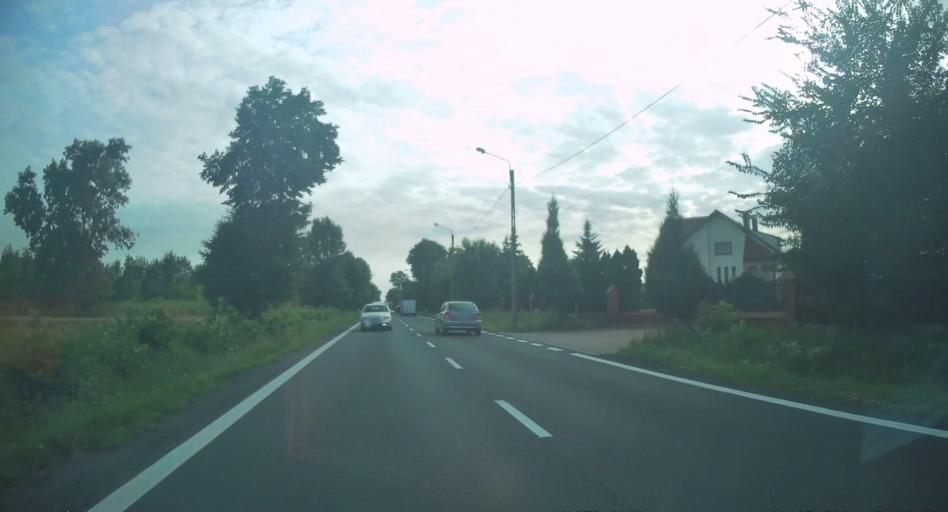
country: PL
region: Silesian Voivodeship
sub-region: Powiat czestochowski
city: Rudniki
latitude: 50.8939
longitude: 19.2743
